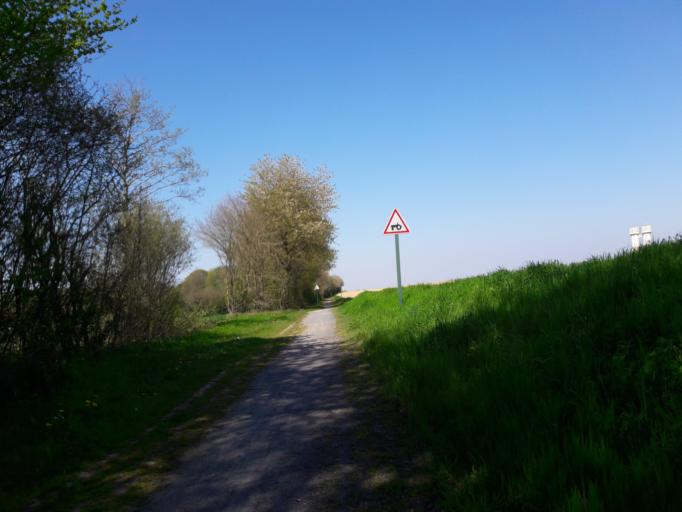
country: FR
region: Nord-Pas-de-Calais
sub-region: Departement du Nord
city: Sains-du-Nord
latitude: 50.1536
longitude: 4.0696
